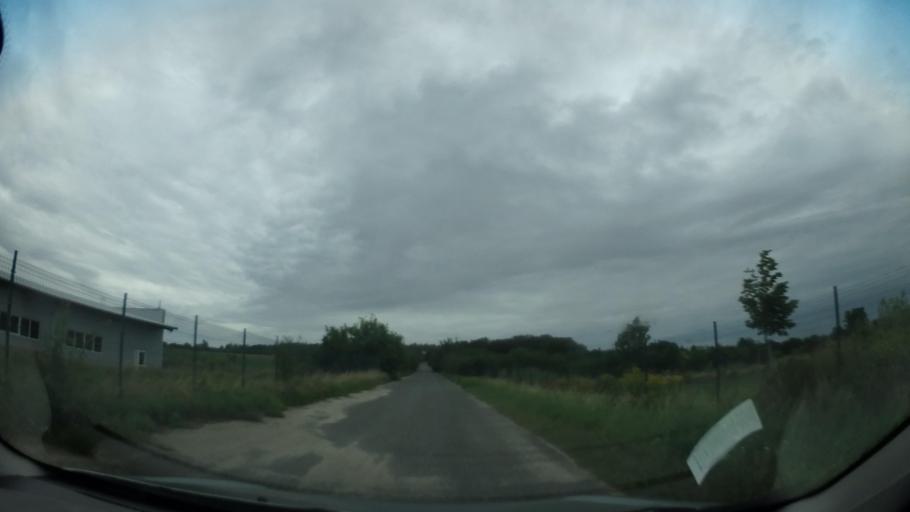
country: CZ
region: Central Bohemia
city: Lysa nad Labem
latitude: 50.2118
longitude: 14.8472
